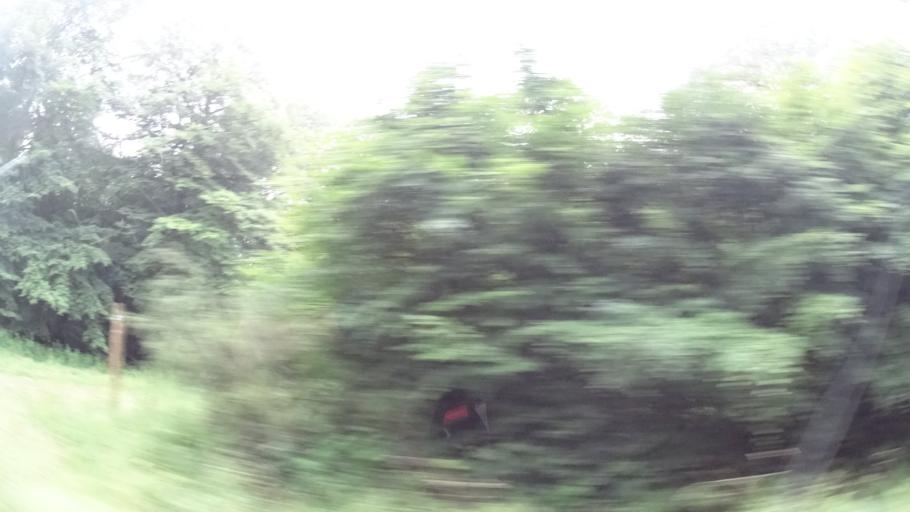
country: BE
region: Wallonia
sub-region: Province du Luxembourg
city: Habay-la-Vieille
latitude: 49.7543
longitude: 5.5999
